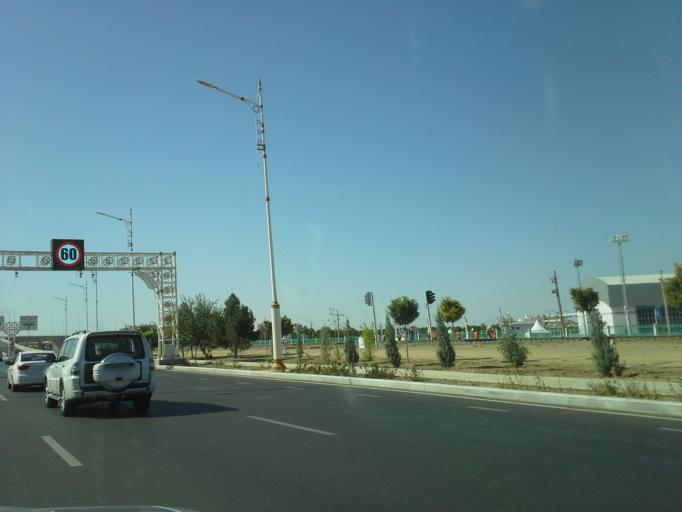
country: TM
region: Ahal
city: Ashgabat
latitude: 37.9237
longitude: 58.4382
